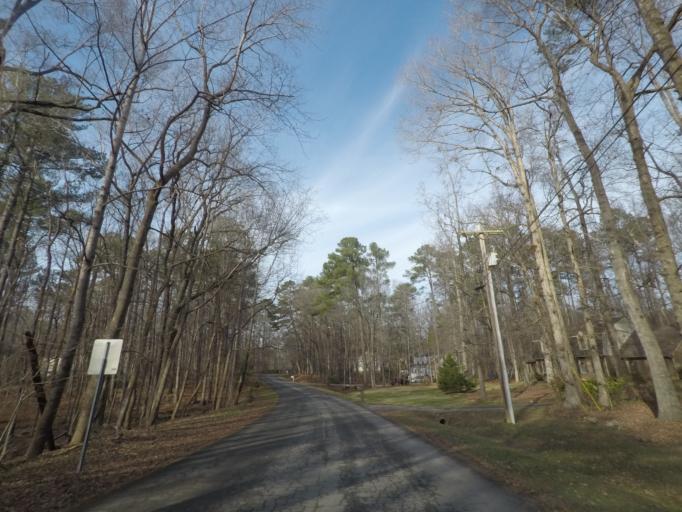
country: US
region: North Carolina
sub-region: Durham County
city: Durham
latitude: 36.0789
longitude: -78.9662
